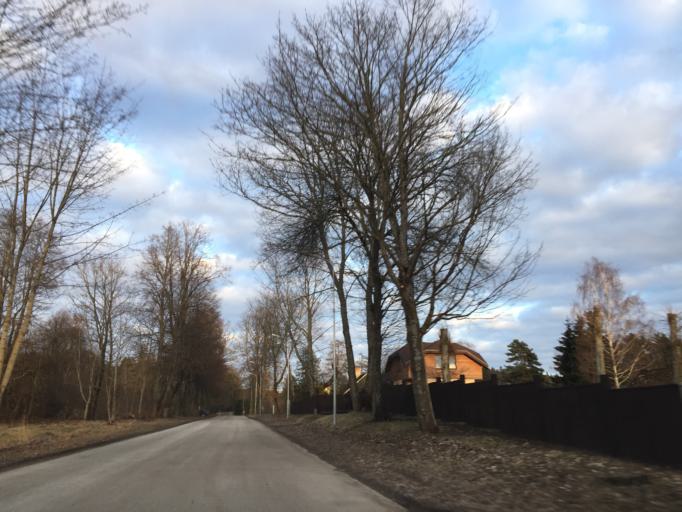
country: LV
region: Babite
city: Pinki
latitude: 56.9206
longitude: 23.8739
